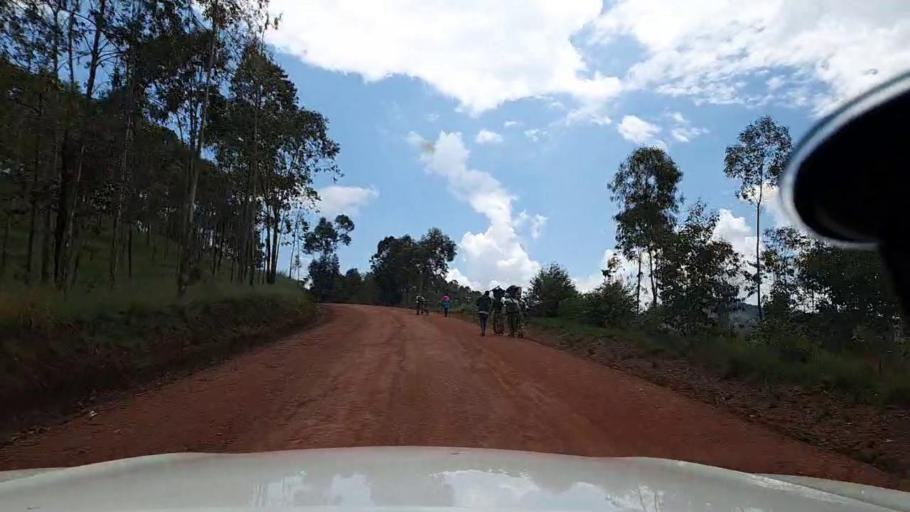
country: RW
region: Kigali
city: Kigali
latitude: -1.7645
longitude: 29.8413
